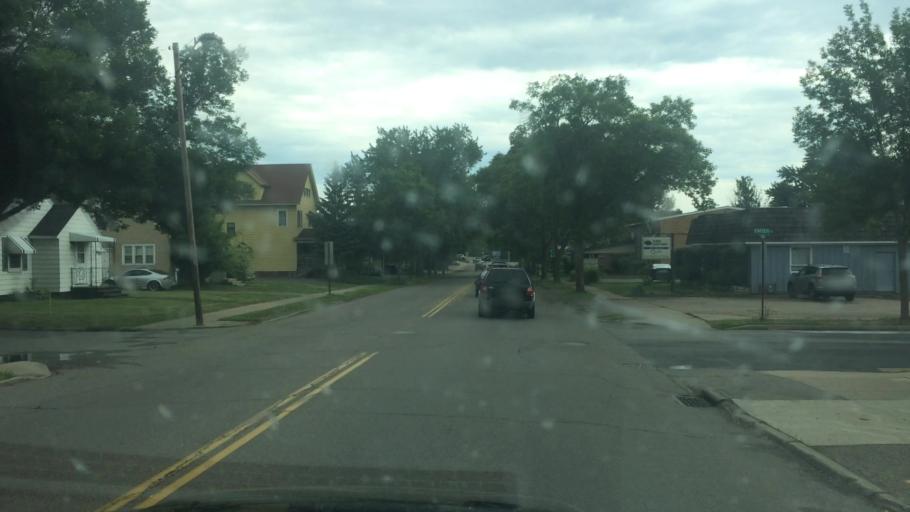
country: US
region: Wisconsin
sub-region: Marathon County
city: Wausau
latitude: 44.9488
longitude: -89.6326
